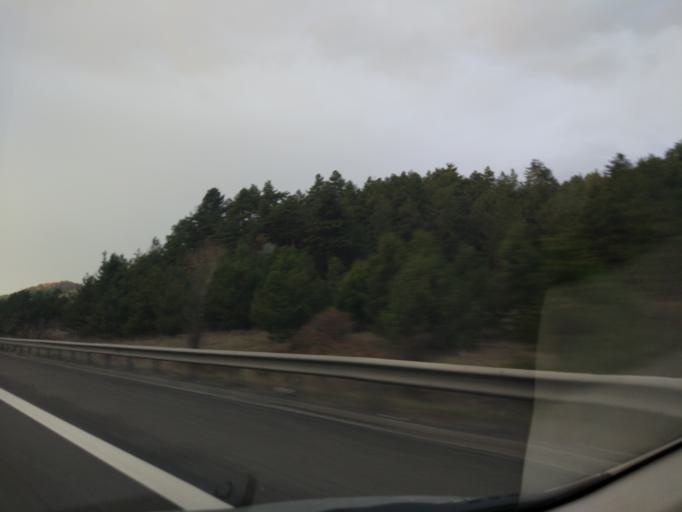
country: TR
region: Bolu
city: Bolu
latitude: 40.7362
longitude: 31.8003
